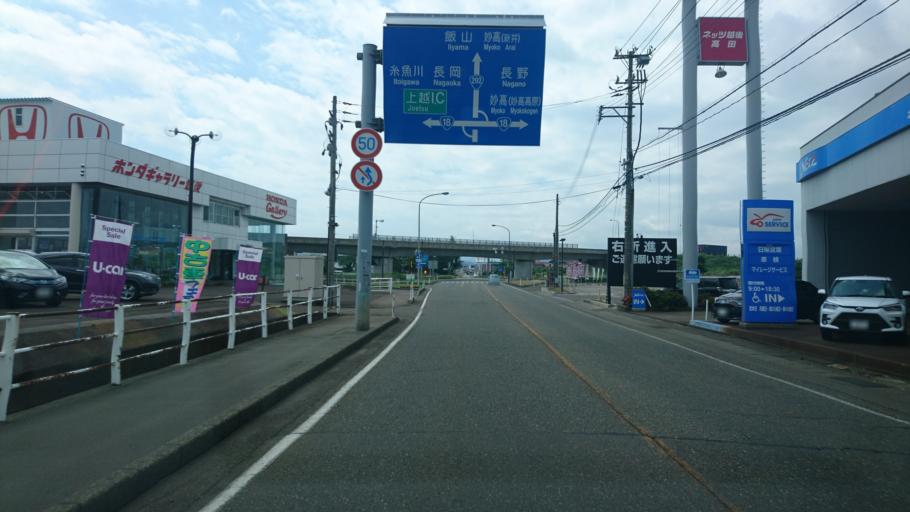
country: JP
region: Niigata
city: Arai
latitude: 37.0610
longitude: 138.2593
